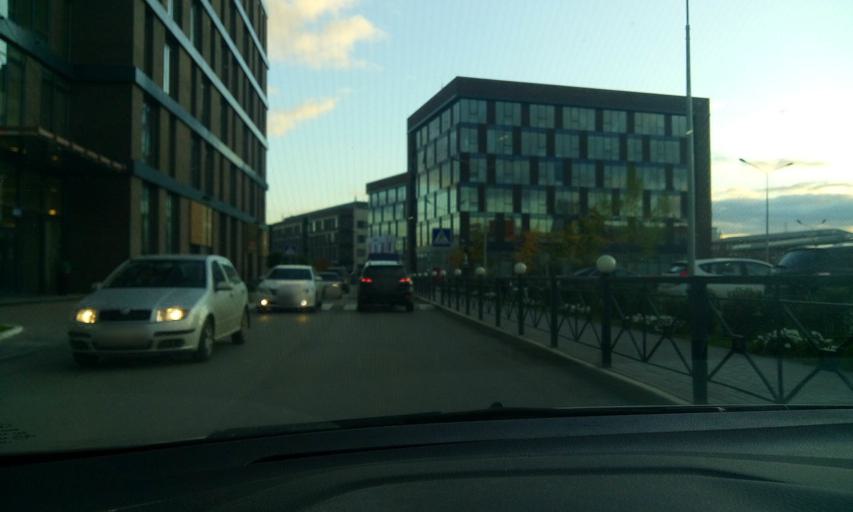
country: RU
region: Sverdlovsk
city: Yekaterinburg
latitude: 56.8229
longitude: 60.6517
